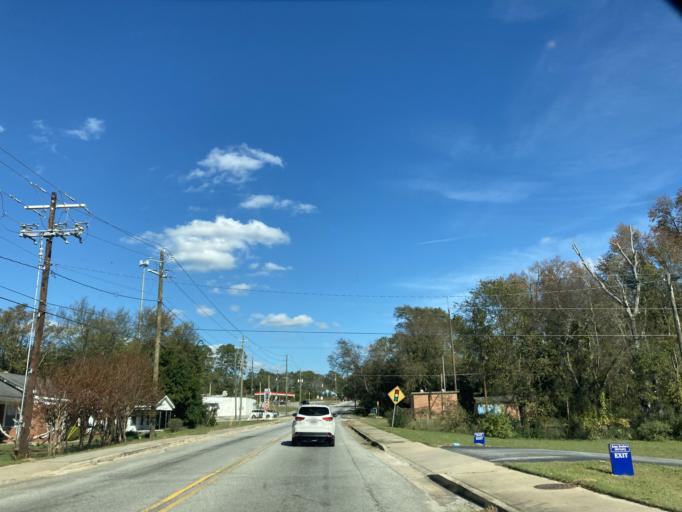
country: US
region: Georgia
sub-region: Bibb County
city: Macon
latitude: 32.8631
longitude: -83.5712
